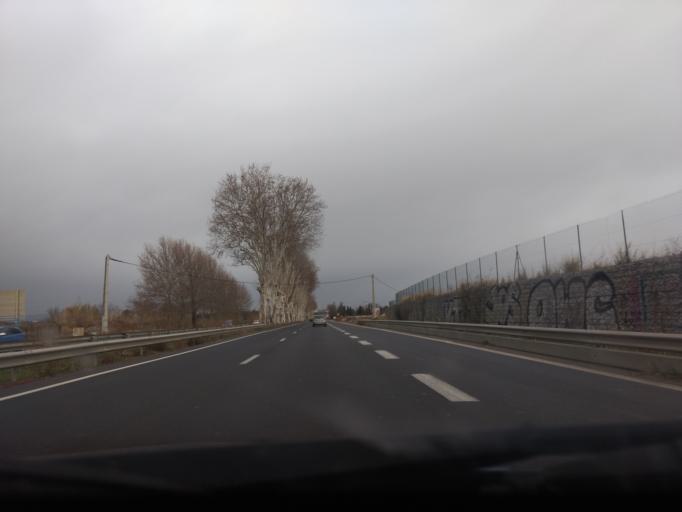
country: FR
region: Languedoc-Roussillon
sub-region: Departement de l'Herault
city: Lattes
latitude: 43.5735
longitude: 3.8968
